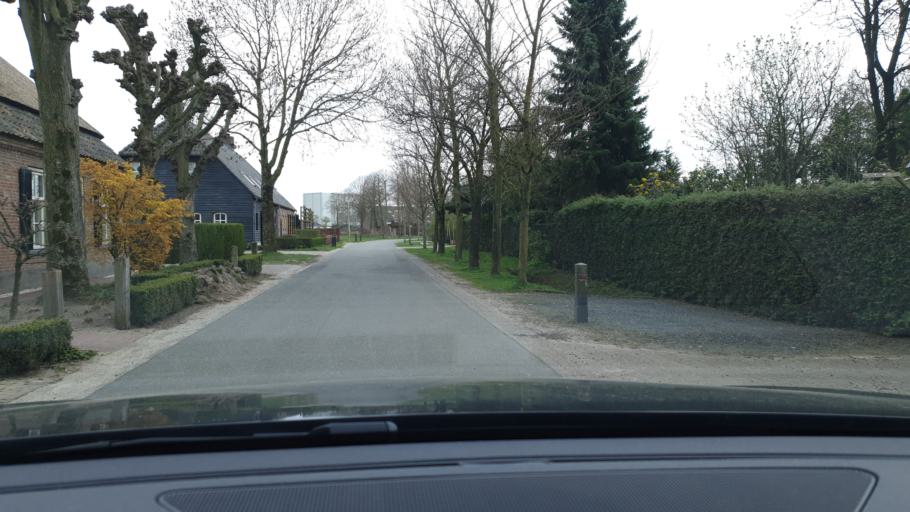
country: NL
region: North Brabant
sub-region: Gemeente Oirschot
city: Oirschot
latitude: 51.5109
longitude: 5.3435
